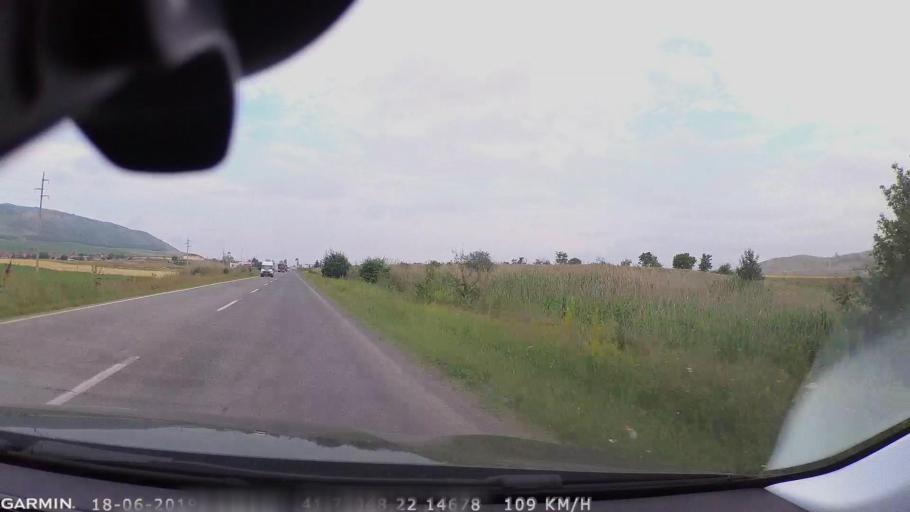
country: MK
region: Stip
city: Shtip
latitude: 41.7710
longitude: 22.1455
